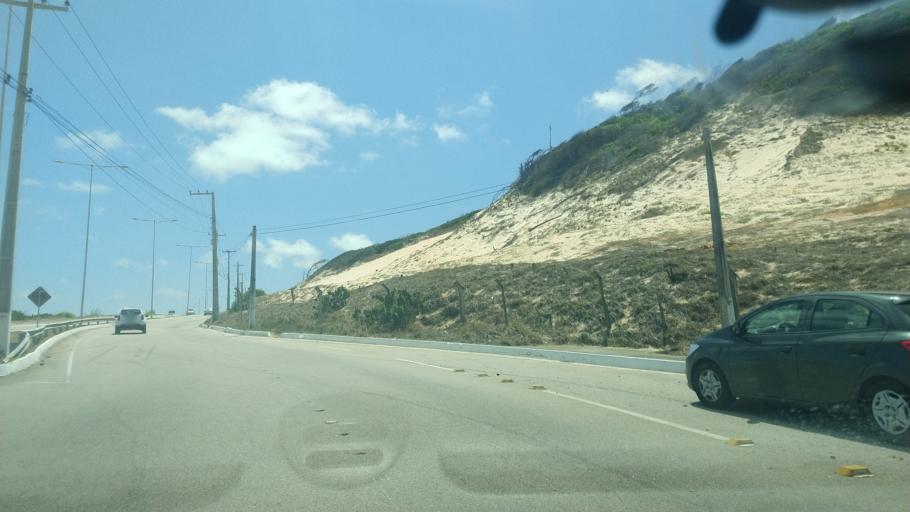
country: BR
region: Rio Grande do Norte
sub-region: Natal
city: Natal
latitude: -5.8169
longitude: -35.1832
